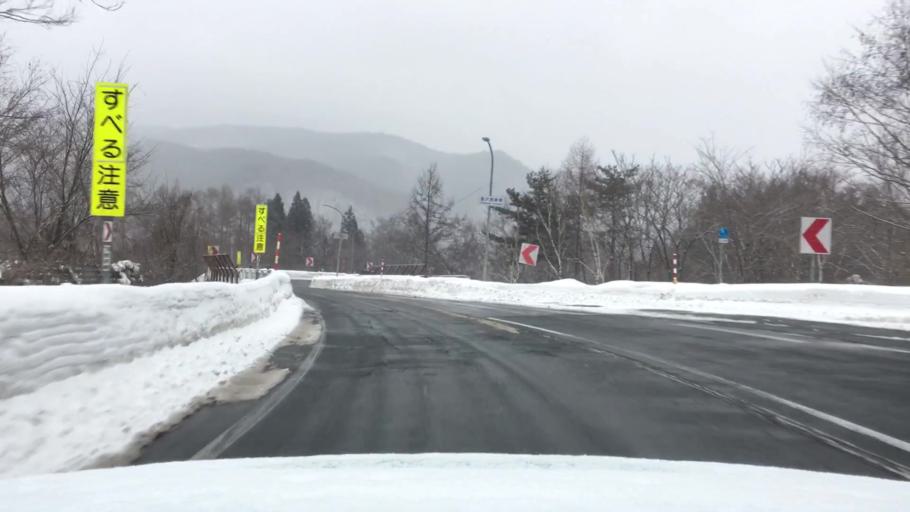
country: JP
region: Akita
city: Hanawa
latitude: 40.0312
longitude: 140.9868
